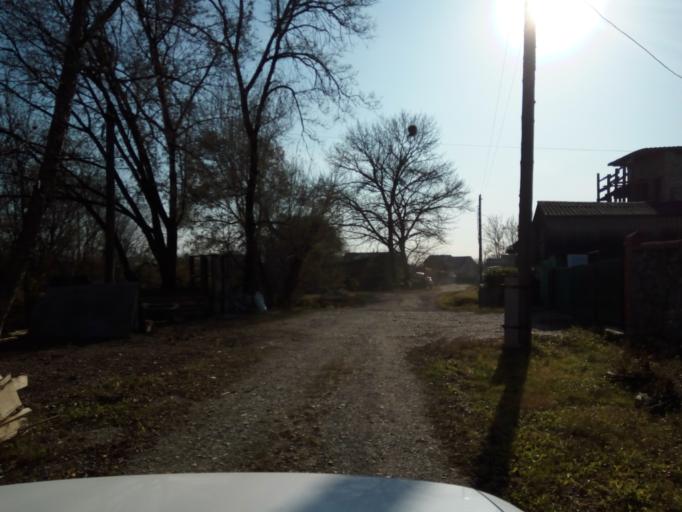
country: RU
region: Primorskiy
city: Dal'nerechensk
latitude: 45.9263
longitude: 133.7263
